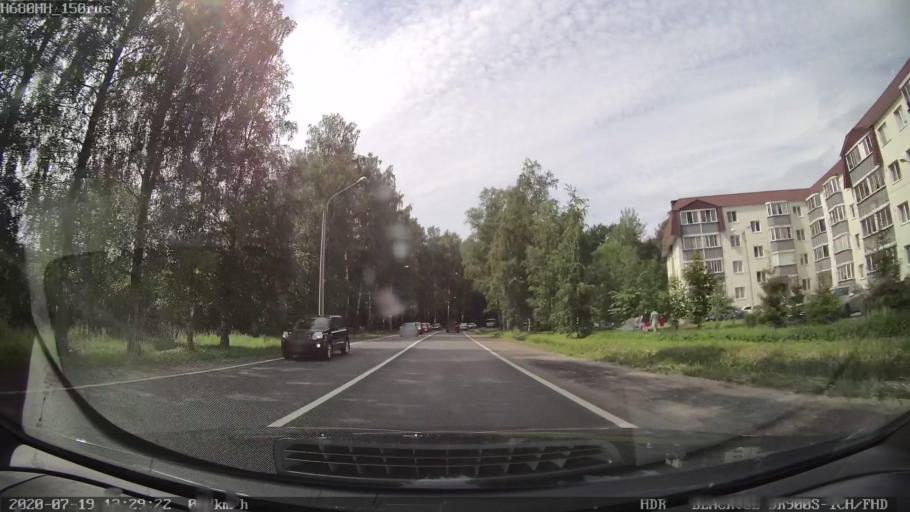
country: RU
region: St.-Petersburg
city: Tyarlevo
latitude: 59.7128
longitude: 30.4316
